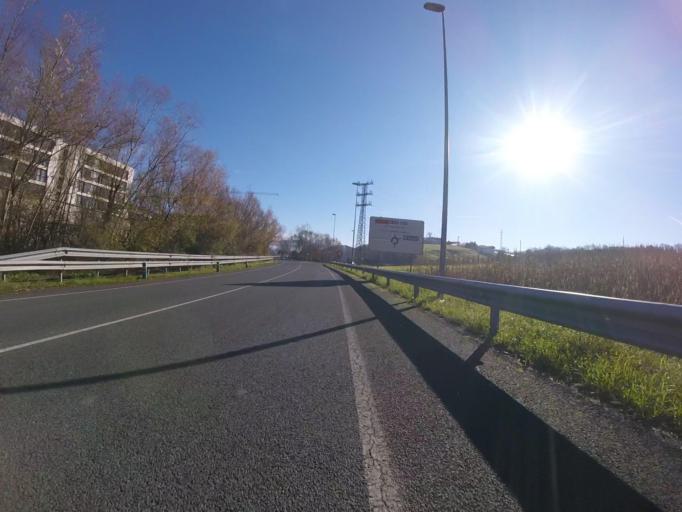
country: ES
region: Basque Country
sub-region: Provincia de Guipuzcoa
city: Fuenterrabia
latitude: 43.3635
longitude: -1.8007
